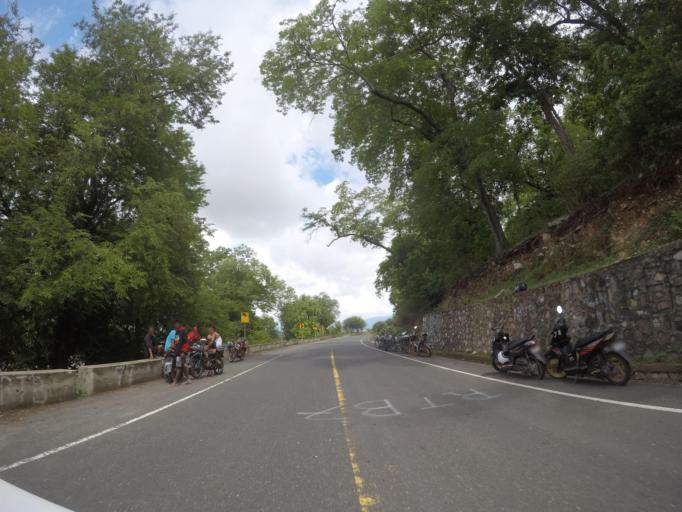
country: TL
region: Liquica
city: Maubara
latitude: -8.7431
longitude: 125.1243
